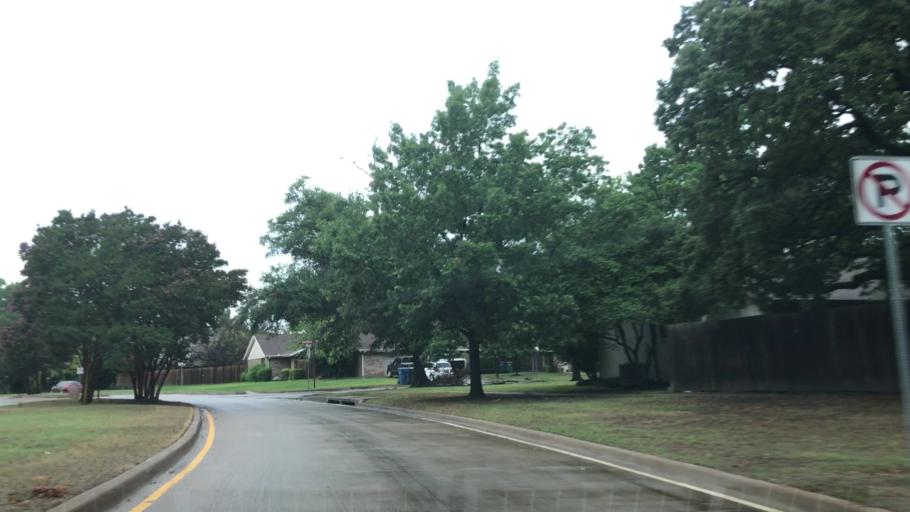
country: US
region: Texas
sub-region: Denton County
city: Highland Village
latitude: 33.0426
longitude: -97.0480
